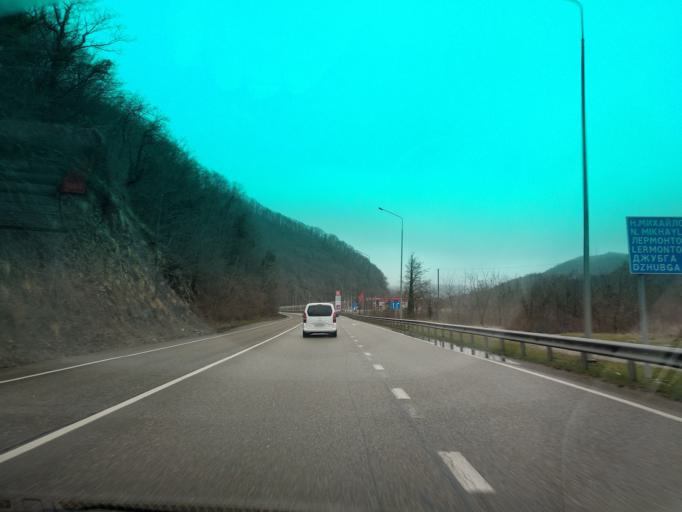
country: RU
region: Krasnodarskiy
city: Ol'ginka
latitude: 44.2153
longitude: 38.8948
